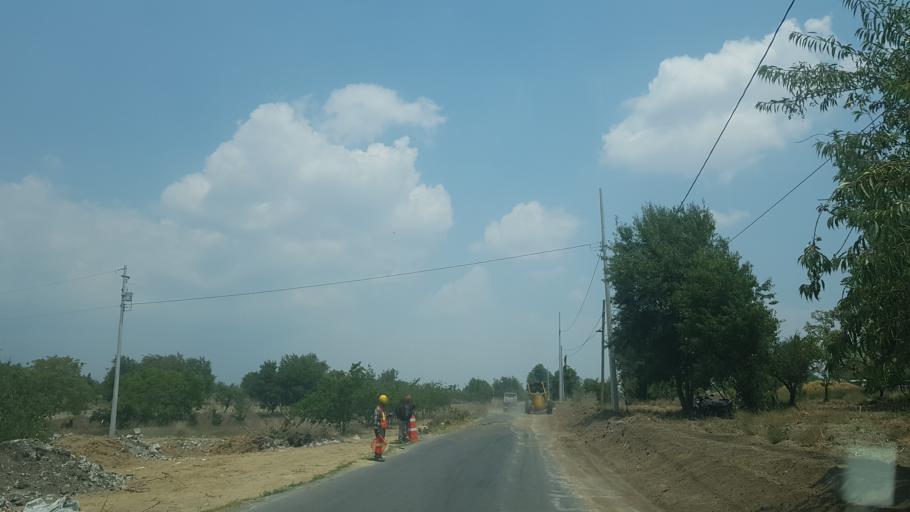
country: MX
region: Puebla
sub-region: San Nicolas de los Ranchos
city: San Pedro Yancuitlalpan
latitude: 19.0854
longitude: -98.4814
